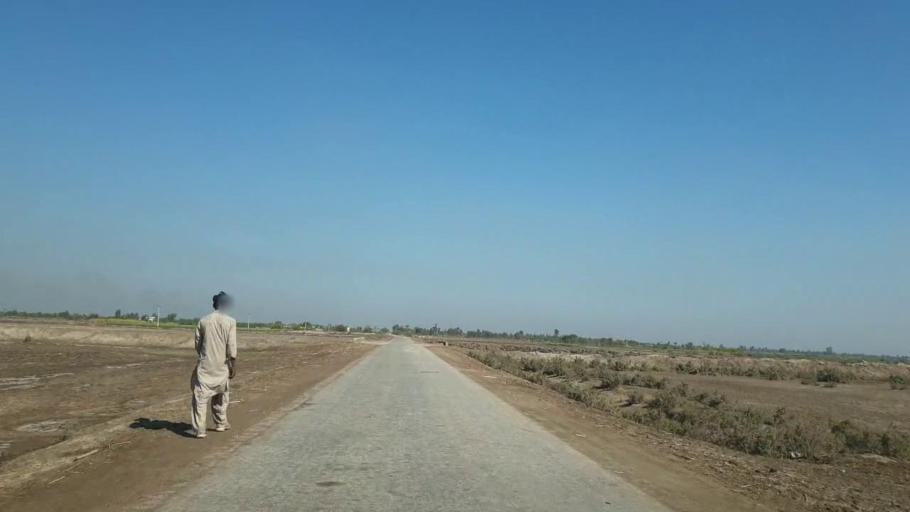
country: PK
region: Sindh
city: Mirpur Khas
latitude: 25.5715
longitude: 69.0463
